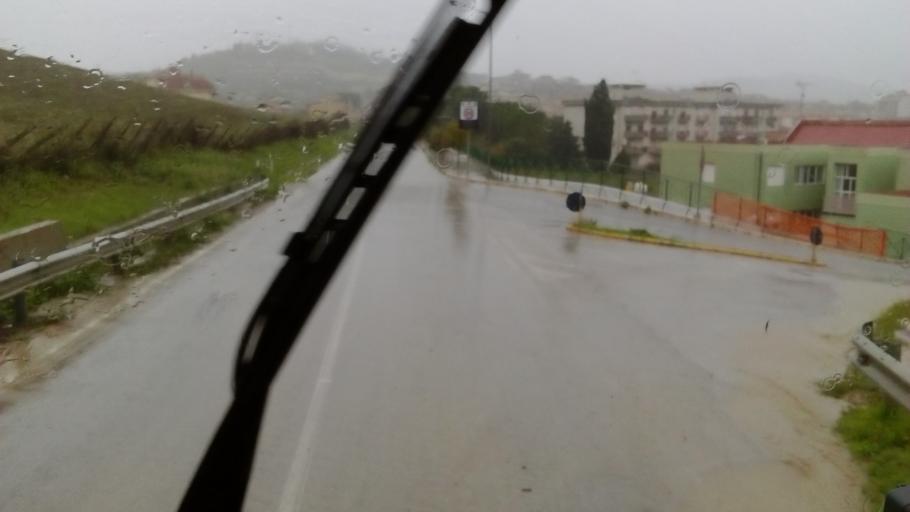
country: IT
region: Sicily
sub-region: Enna
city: Pietraperzia
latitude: 37.4181
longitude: 14.1457
